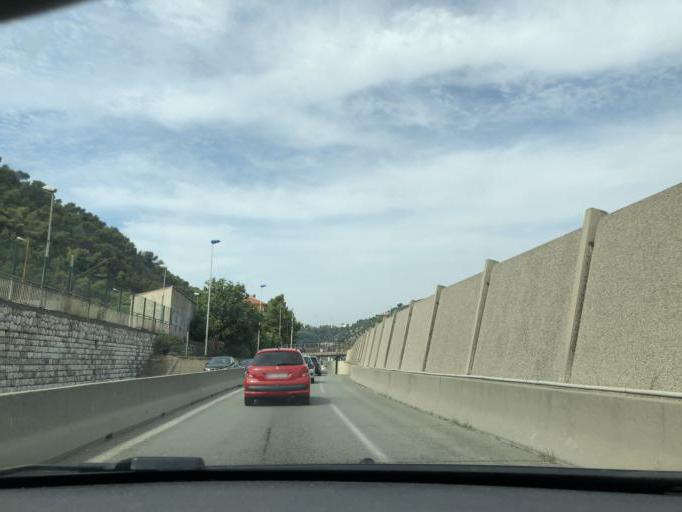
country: FR
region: Provence-Alpes-Cote d'Azur
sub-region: Departement des Alpes-Maritimes
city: La Trinite
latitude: 43.7346
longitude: 7.3031
